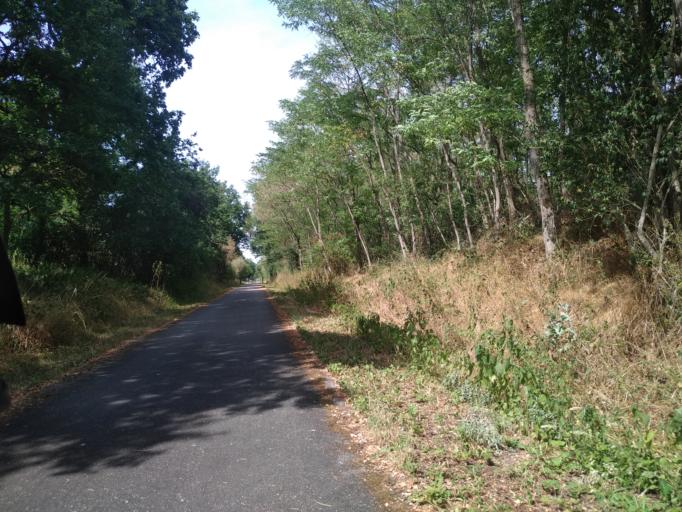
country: FR
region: Auvergne
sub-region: Departement de l'Allier
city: Diou
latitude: 46.5554
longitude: 3.7442
